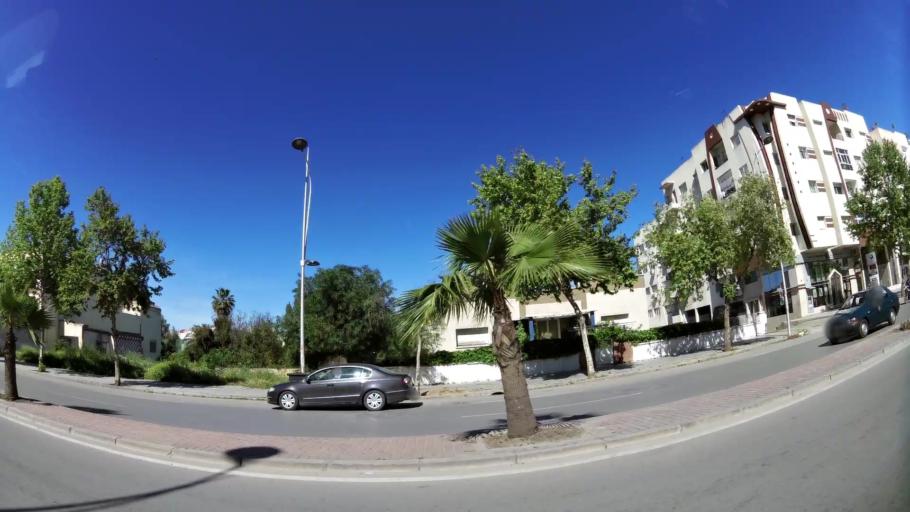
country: MA
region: Fes-Boulemane
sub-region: Fes
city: Fes
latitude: 34.0256
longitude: -4.9904
